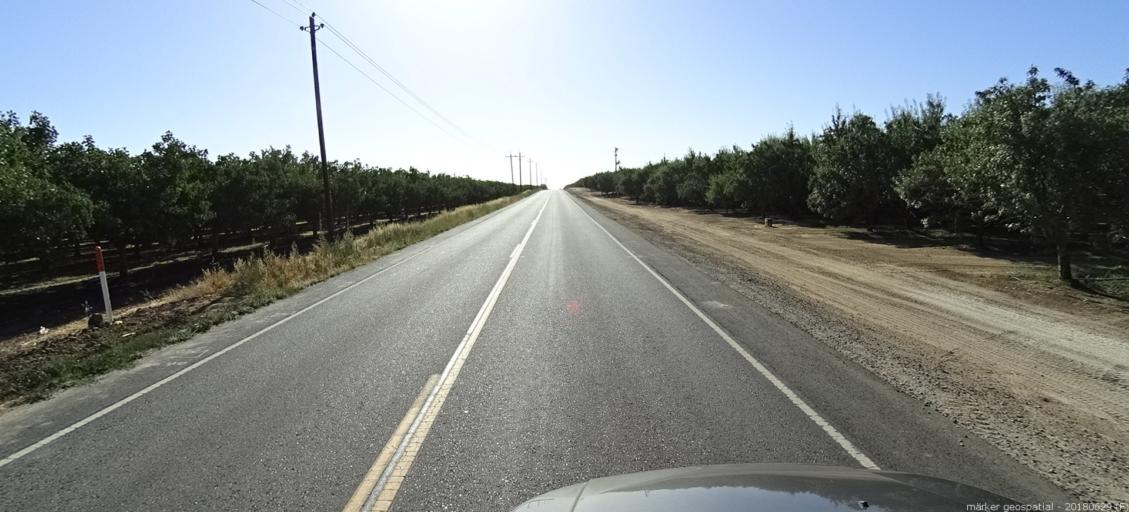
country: US
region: California
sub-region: Madera County
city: Parksdale
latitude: 36.9666
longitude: -119.9627
